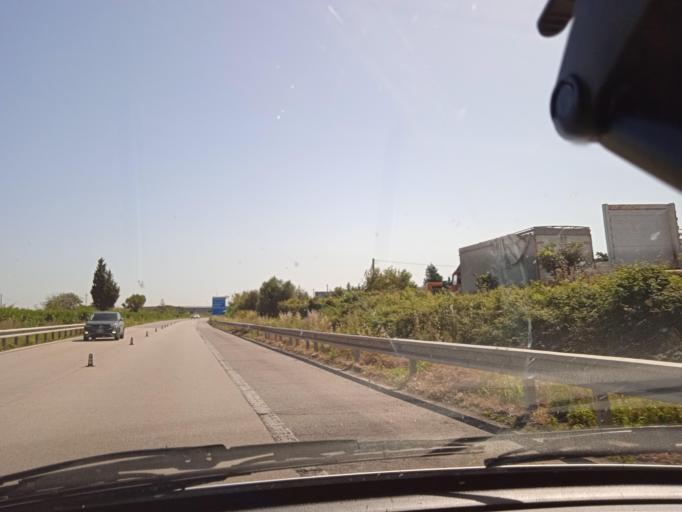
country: IT
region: Sicily
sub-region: Messina
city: Terme
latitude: 38.1519
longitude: 15.1801
